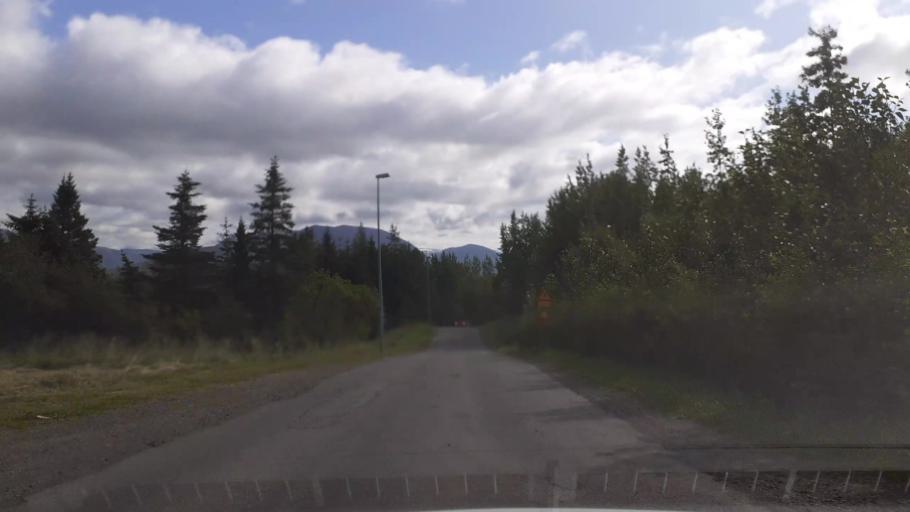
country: IS
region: Northeast
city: Akureyri
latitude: 65.6480
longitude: -18.0875
